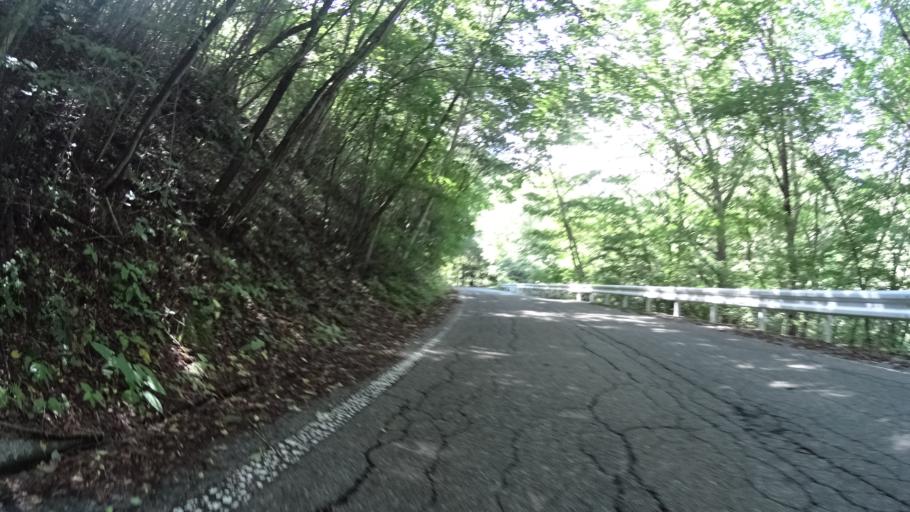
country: JP
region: Yamanashi
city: Nirasaki
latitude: 35.9071
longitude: 138.5417
